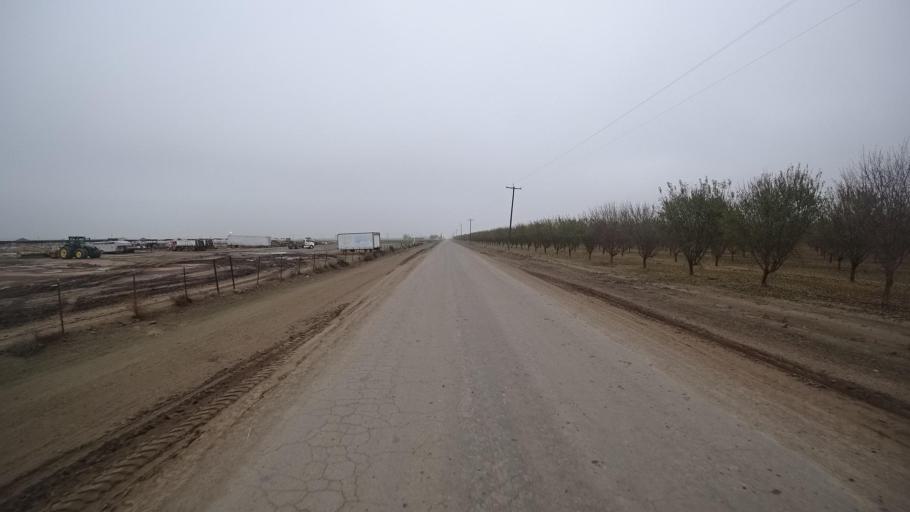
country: US
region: California
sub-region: Kern County
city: Wasco
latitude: 35.7120
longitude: -119.4195
